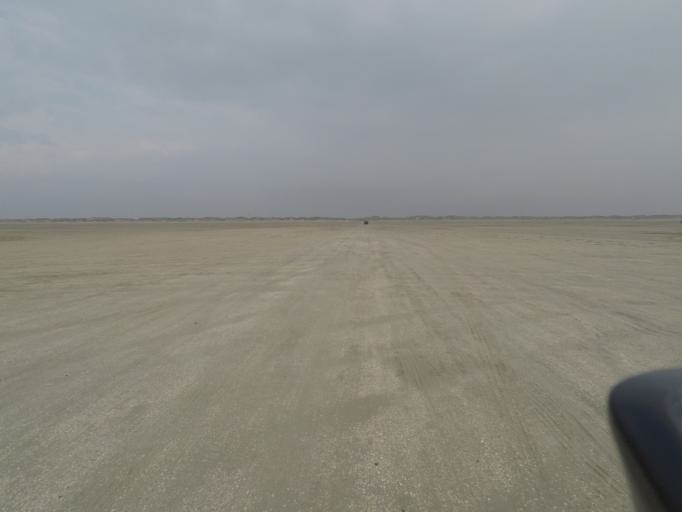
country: DE
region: Schleswig-Holstein
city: List
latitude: 55.1474
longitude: 8.4805
